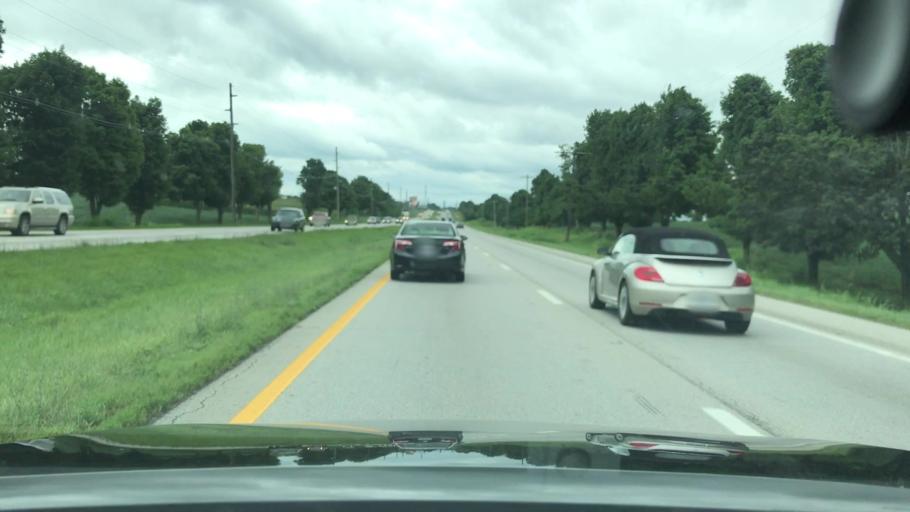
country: US
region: Ohio
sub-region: Franklin County
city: Obetz
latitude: 39.8483
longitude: -83.0020
